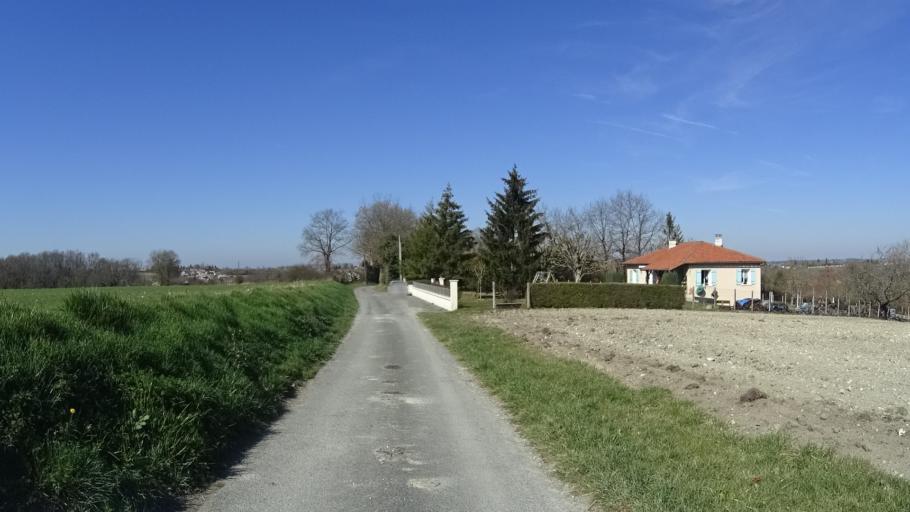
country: FR
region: Aquitaine
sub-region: Departement de la Dordogne
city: Riberac
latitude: 45.2315
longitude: 0.3429
